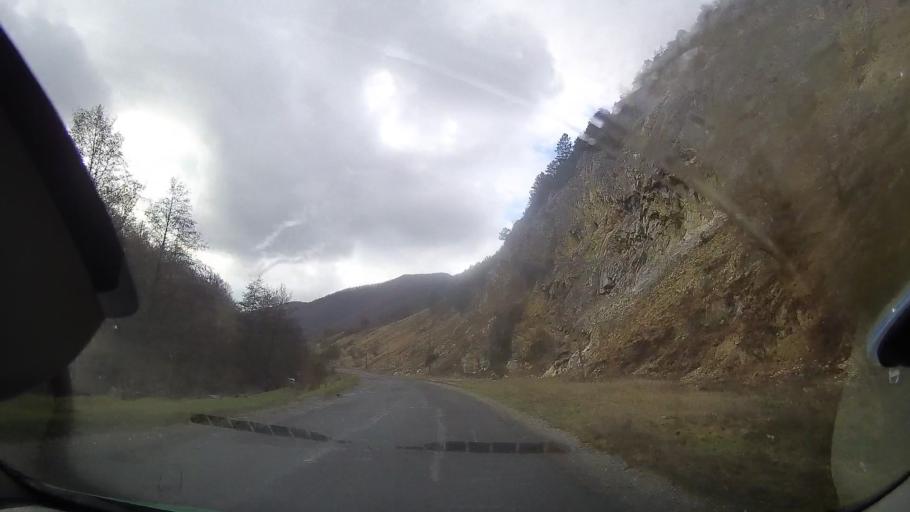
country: RO
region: Alba
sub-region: Comuna Rimetea
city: Rimetea
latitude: 46.5018
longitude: 23.5920
